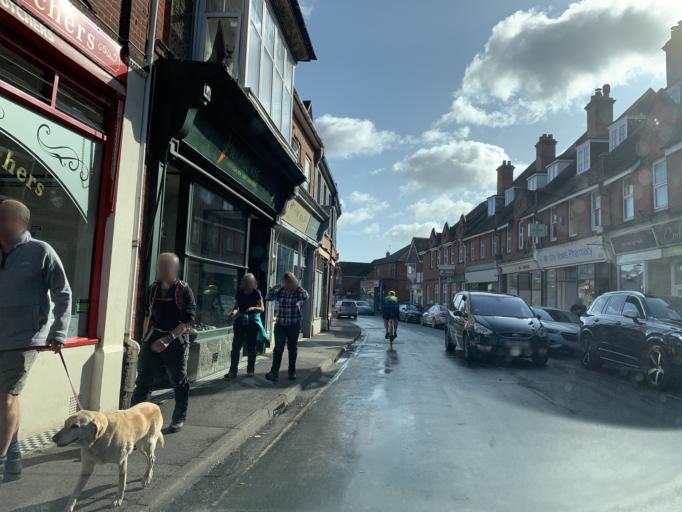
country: GB
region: England
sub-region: Hampshire
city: Brockenhurst
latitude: 50.8193
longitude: -1.5781
